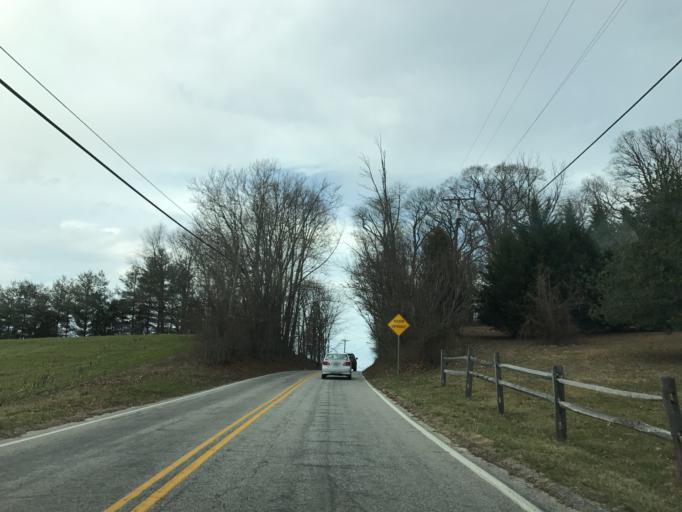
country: US
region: Maryland
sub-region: Harford County
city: South Bel Air
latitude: 39.5717
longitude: -76.2917
